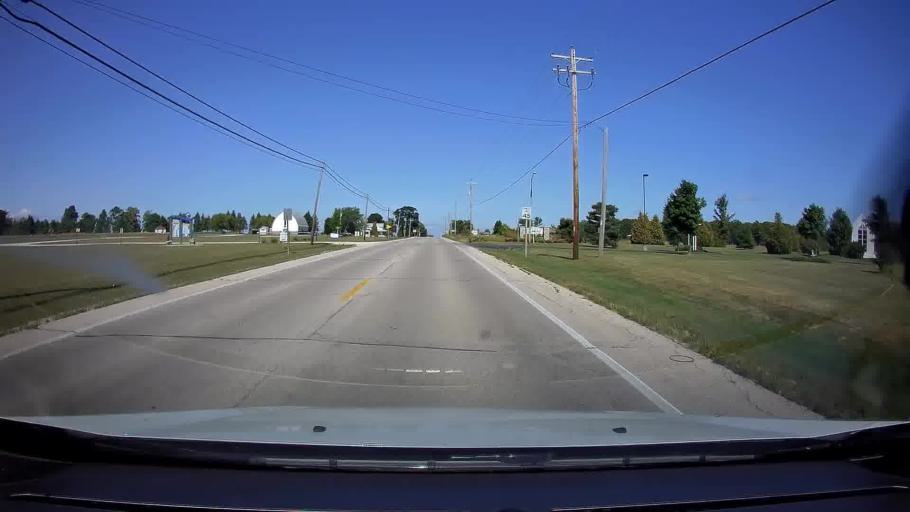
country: US
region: Michigan
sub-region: Delta County
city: Escanaba
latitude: 45.2452
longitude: -87.0861
